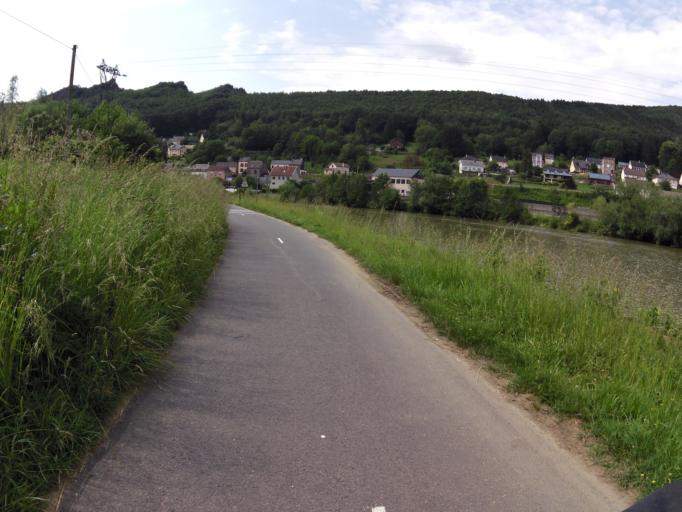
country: FR
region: Champagne-Ardenne
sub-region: Departement des Ardennes
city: Montherme
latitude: 49.8605
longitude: 4.7509
